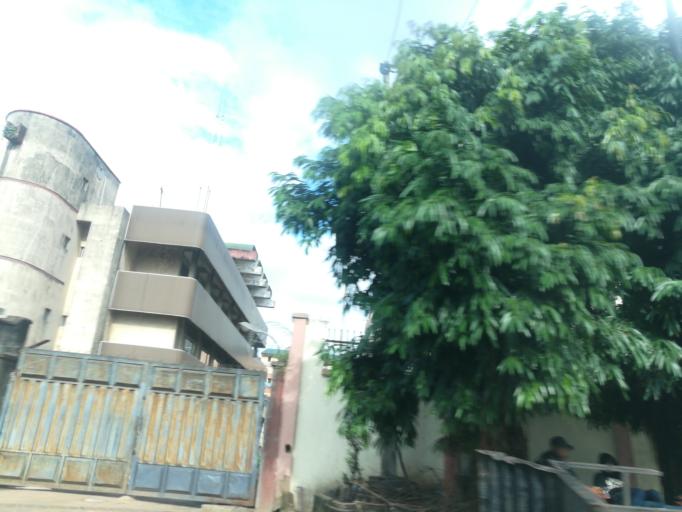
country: NG
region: Lagos
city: Ikeja
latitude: 6.6219
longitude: 3.3564
